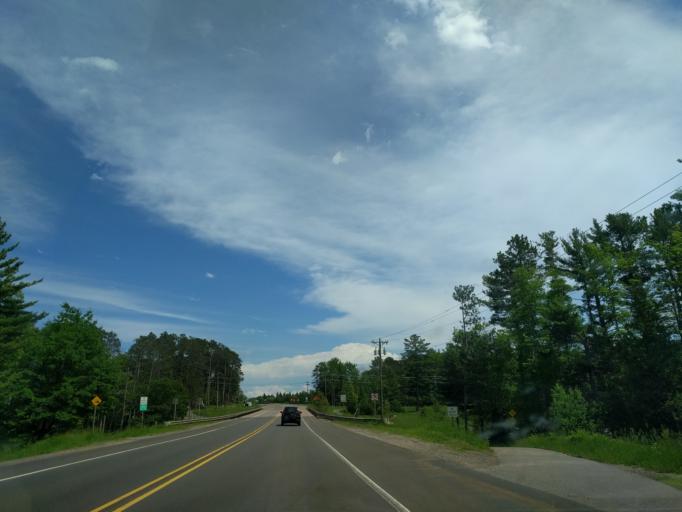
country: US
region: Michigan
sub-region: Marquette County
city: Trowbridge Park
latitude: 46.5724
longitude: -87.4116
